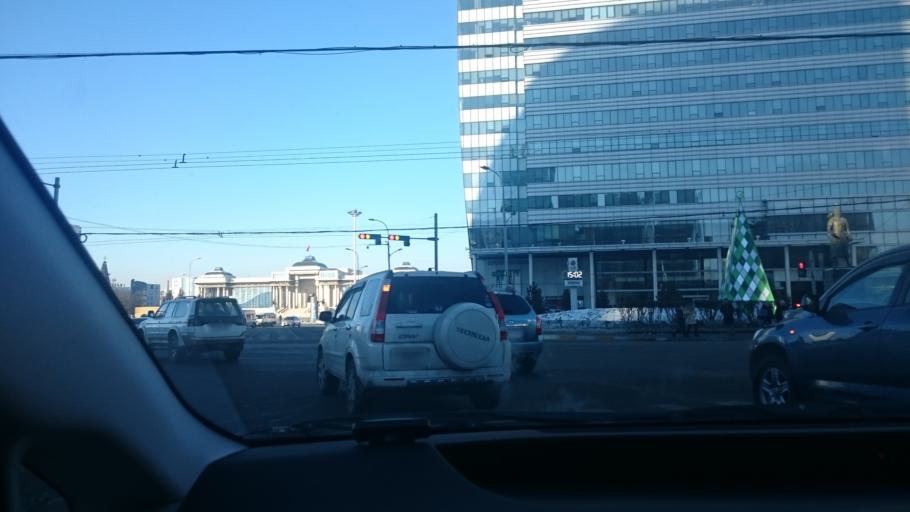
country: MN
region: Ulaanbaatar
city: Ulaanbaatar
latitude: 47.9170
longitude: 106.9200
